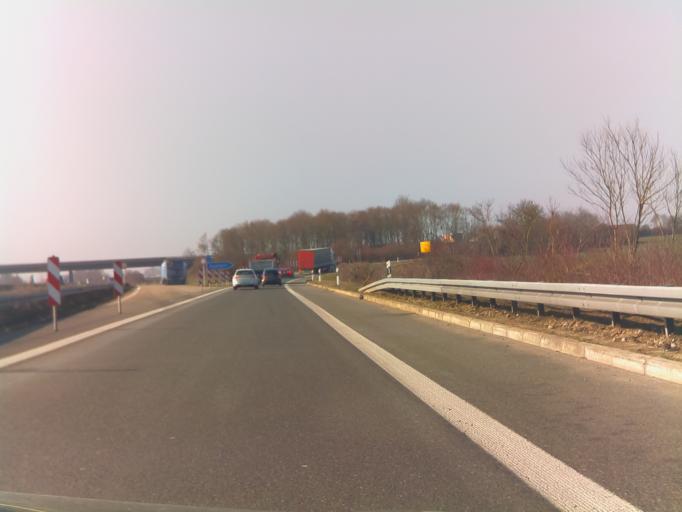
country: DE
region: Baden-Wuerttemberg
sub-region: Regierungsbezirk Stuttgart
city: Bondorf
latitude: 48.5053
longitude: 8.8456
